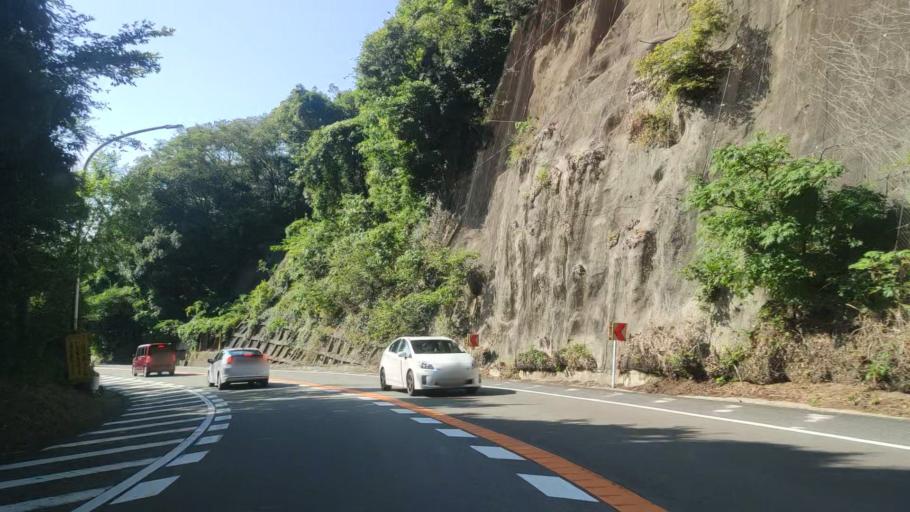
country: JP
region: Hyogo
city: Kobe
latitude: 34.6945
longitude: 135.1656
